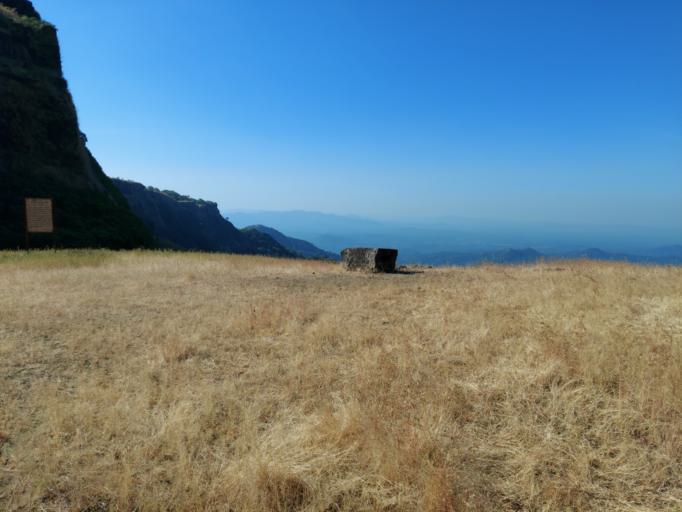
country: IN
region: Maharashtra
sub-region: Sindhudurg
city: Kudal
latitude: 16.0859
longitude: 73.8431
